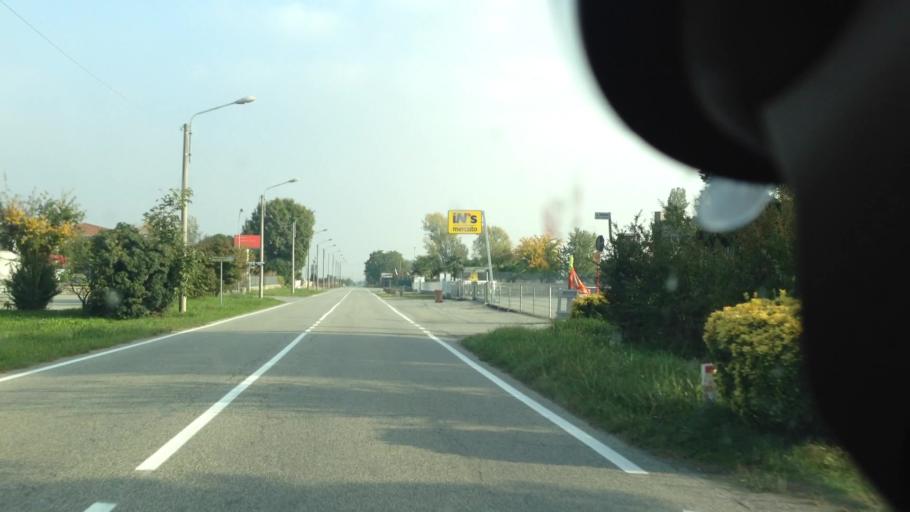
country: IT
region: Piedmont
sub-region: Provincia di Vercelli
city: Cigliano
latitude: 45.3033
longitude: 8.0312
